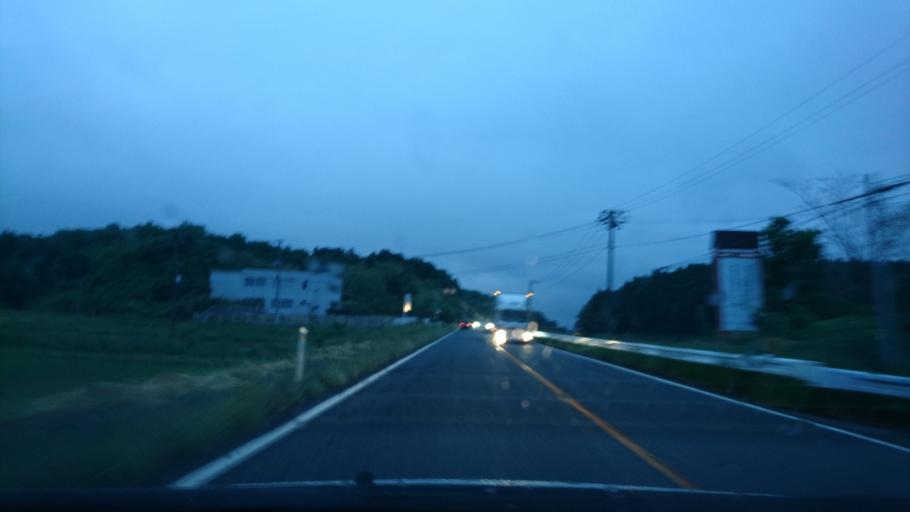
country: JP
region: Iwate
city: Ichinoseki
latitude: 38.7896
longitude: 141.0507
